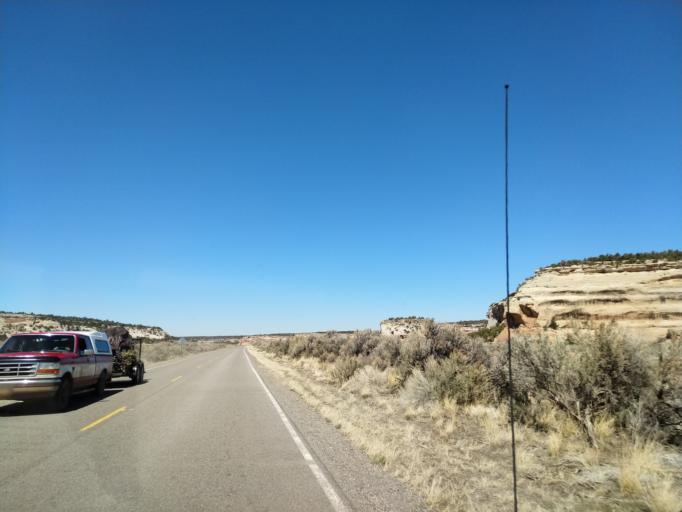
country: US
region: Colorado
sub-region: Mesa County
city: Fruita
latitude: 38.9935
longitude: -108.8227
